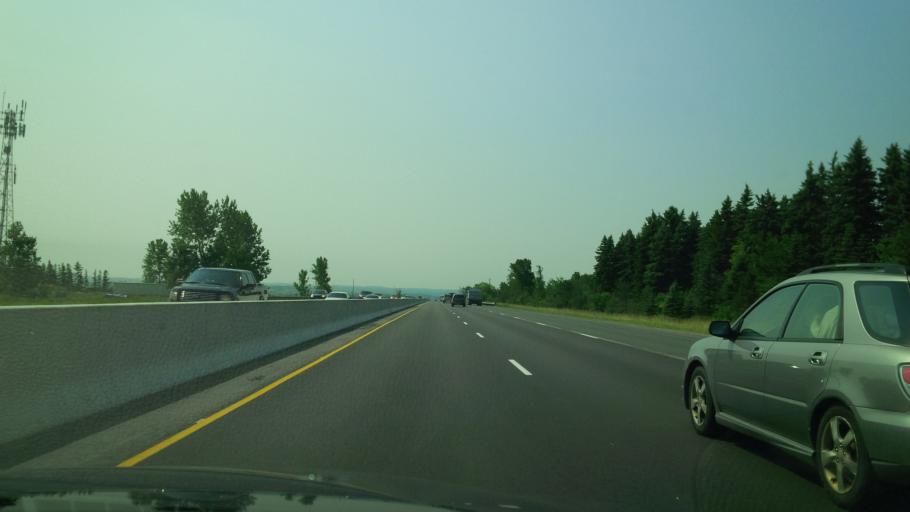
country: CA
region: Ontario
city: Bradford West Gwillimbury
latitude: 44.1273
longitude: -79.6378
